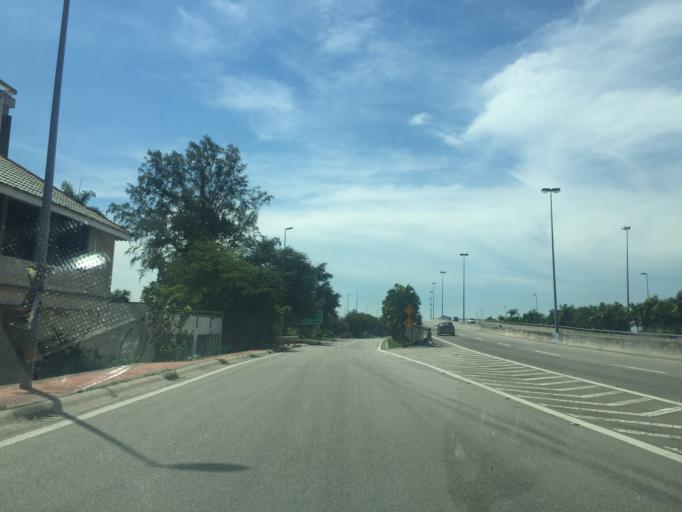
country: MY
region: Penang
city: Butterworth
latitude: 5.4101
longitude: 100.3689
